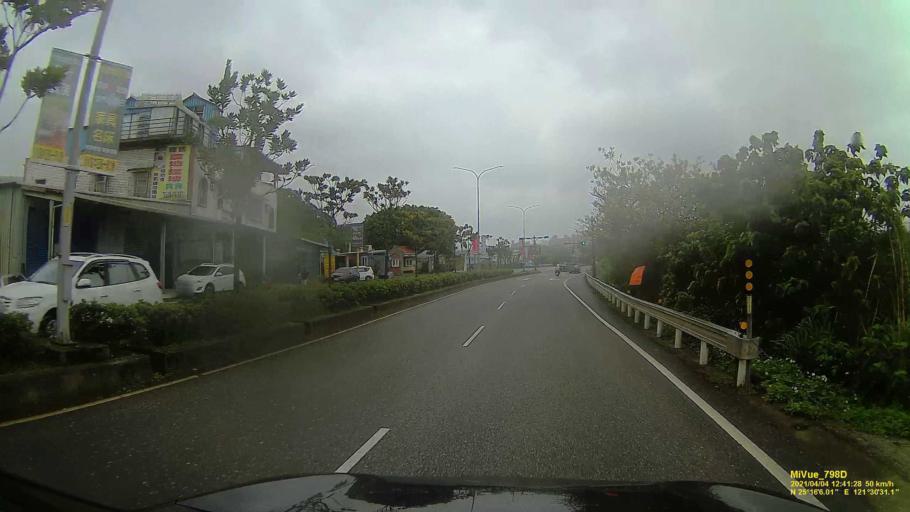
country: TW
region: Taipei
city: Taipei
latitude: 25.2681
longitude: 121.5086
